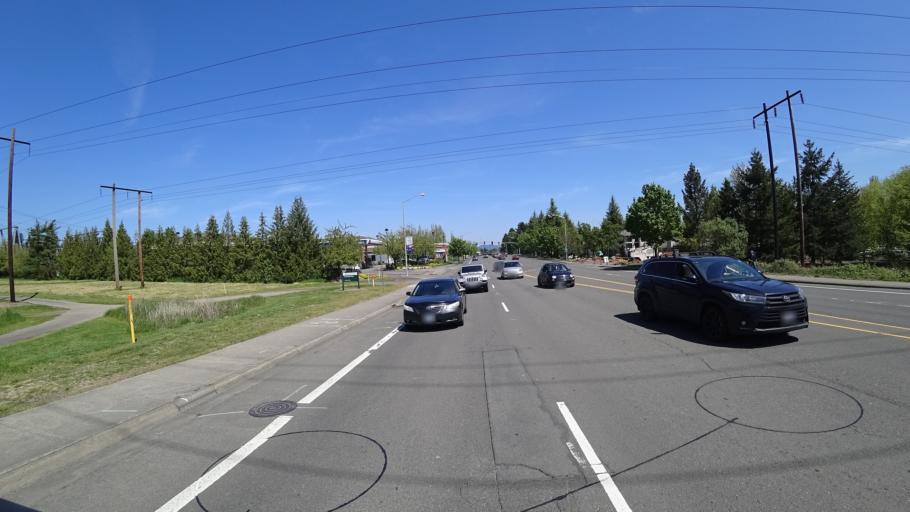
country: US
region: Oregon
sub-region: Washington County
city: King City
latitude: 45.4360
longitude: -122.8305
